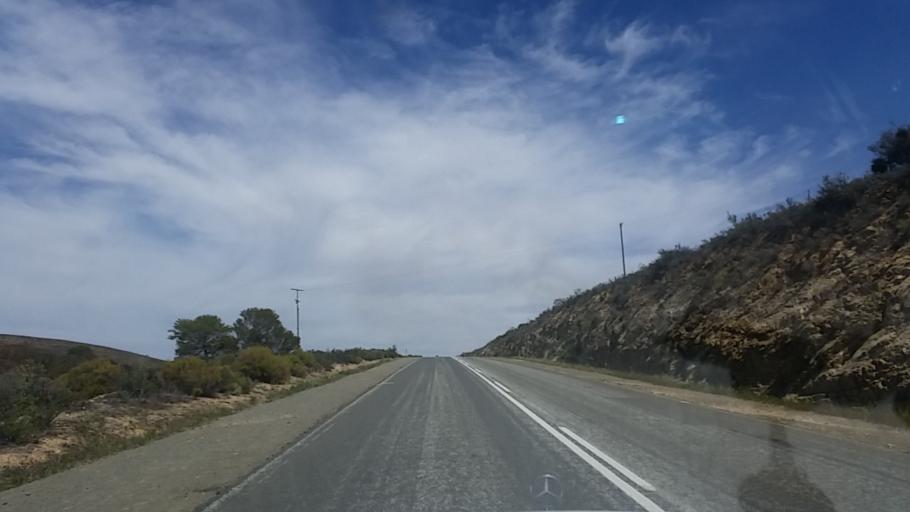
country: ZA
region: Western Cape
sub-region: Eden District Municipality
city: Knysna
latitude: -33.6560
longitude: 23.1185
